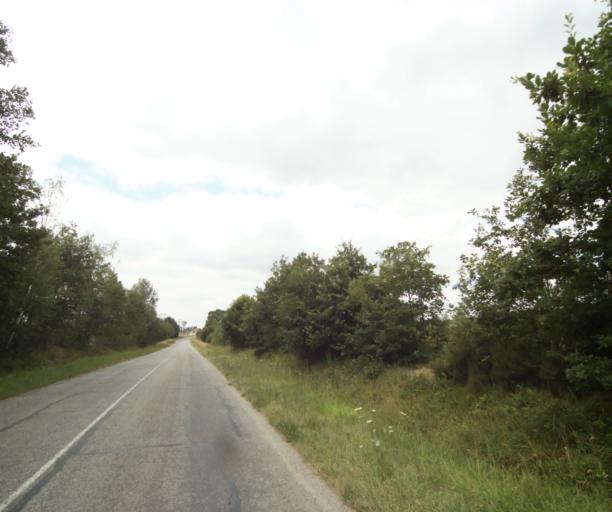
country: FR
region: Centre
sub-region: Departement du Loiret
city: Chanteau
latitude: 47.9634
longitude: 1.9806
